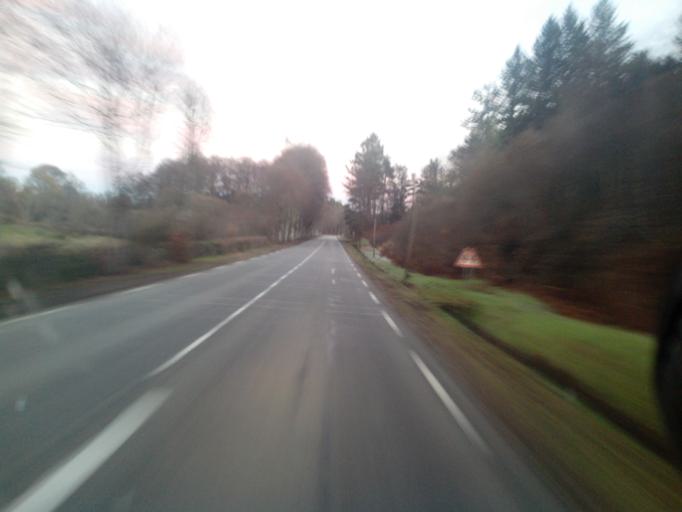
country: FR
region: Limousin
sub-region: Departement de la Correze
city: Meymac
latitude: 45.5147
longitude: 2.1802
